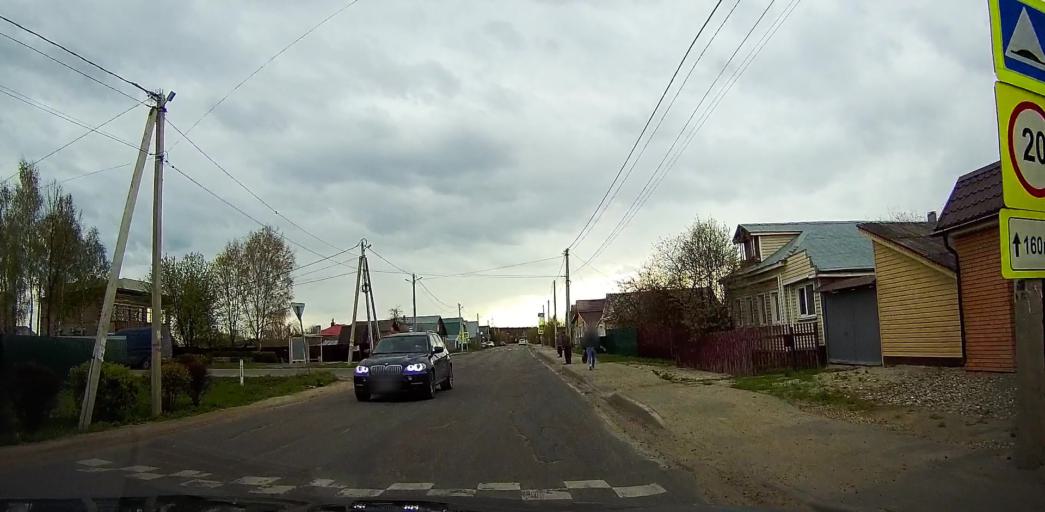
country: RU
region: Moskovskaya
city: Pavlovskiy Posad
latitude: 55.7550
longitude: 38.7044
